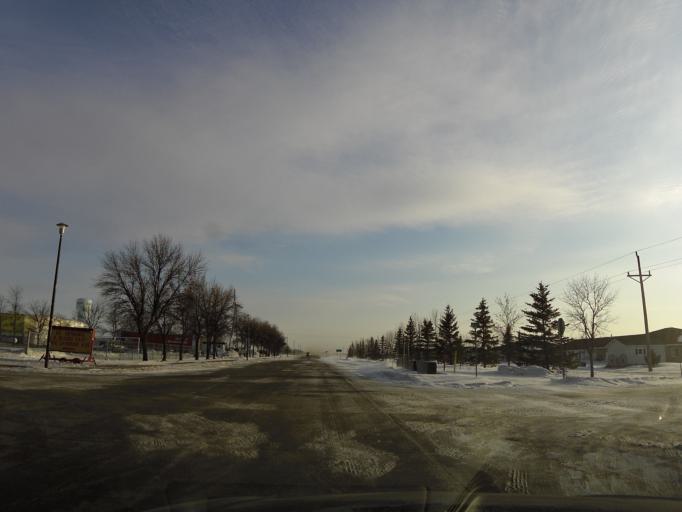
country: US
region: North Dakota
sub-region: Walsh County
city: Grafton
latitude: 48.4084
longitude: -97.4267
